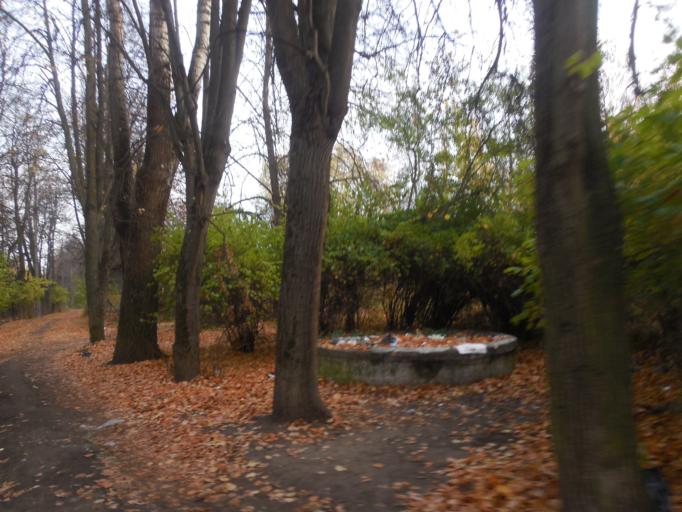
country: RU
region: Moskovskaya
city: Shcherbinka
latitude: 55.4960
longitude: 37.5867
